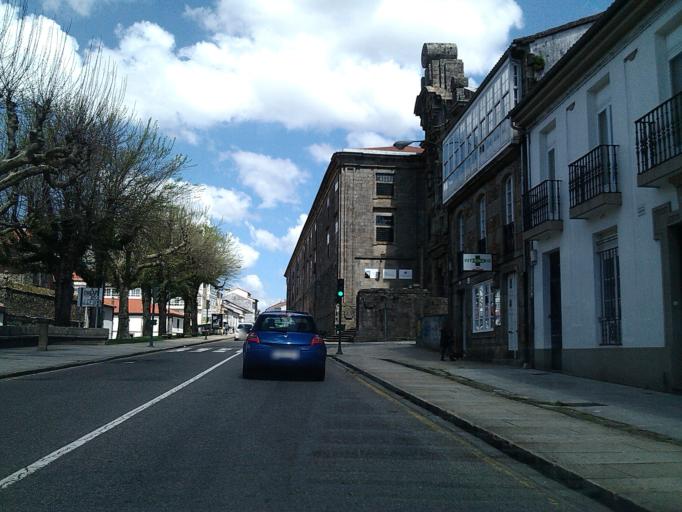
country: ES
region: Galicia
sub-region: Provincia da Coruna
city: Santiago de Compostela
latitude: 42.8844
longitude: -8.5415
